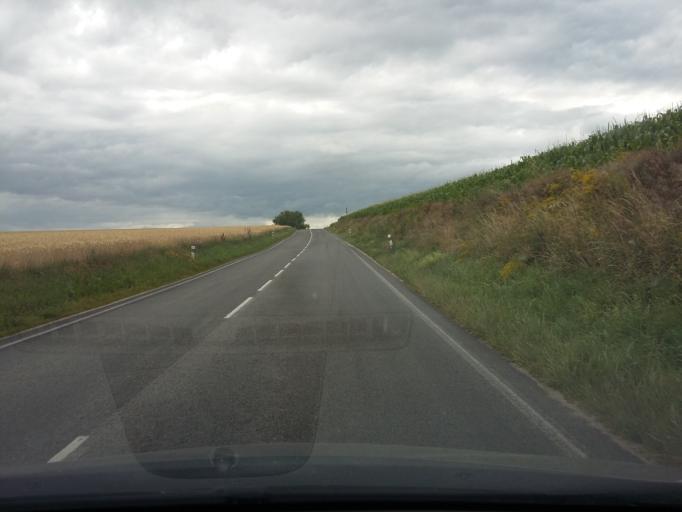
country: SK
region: Trnavsky
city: Vrbove
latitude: 48.5961
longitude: 17.6774
